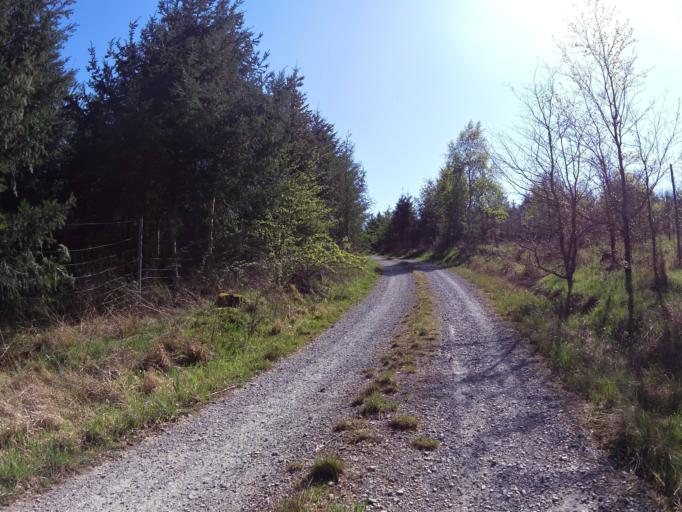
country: DE
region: Thuringia
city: Krauthausen
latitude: 50.9769
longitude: 10.2583
